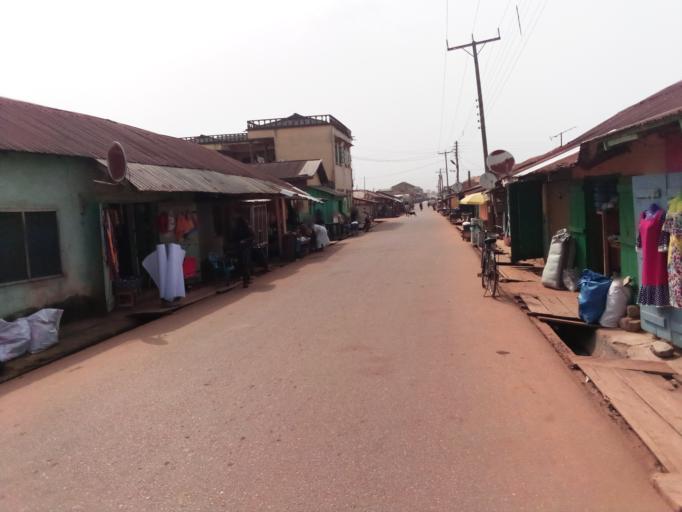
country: CI
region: Sud-Comoe
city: Ayame
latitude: 5.8231
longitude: -2.8198
